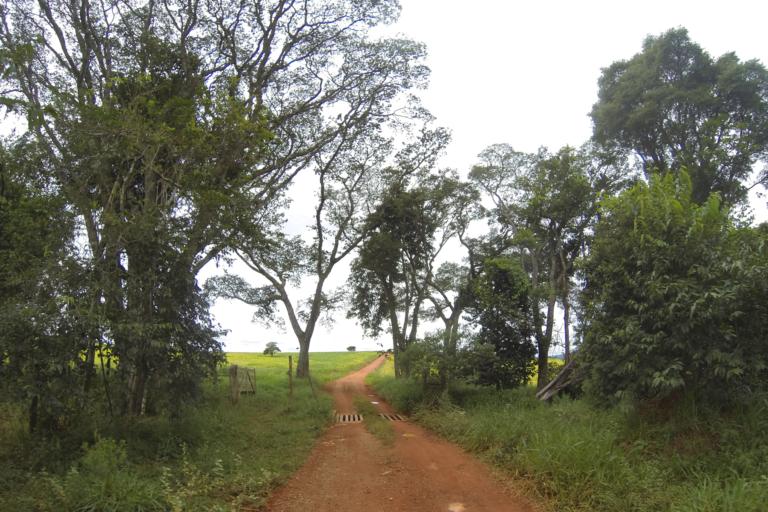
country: BR
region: Minas Gerais
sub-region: Ibia
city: Ibia
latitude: -19.7352
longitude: -46.5639
